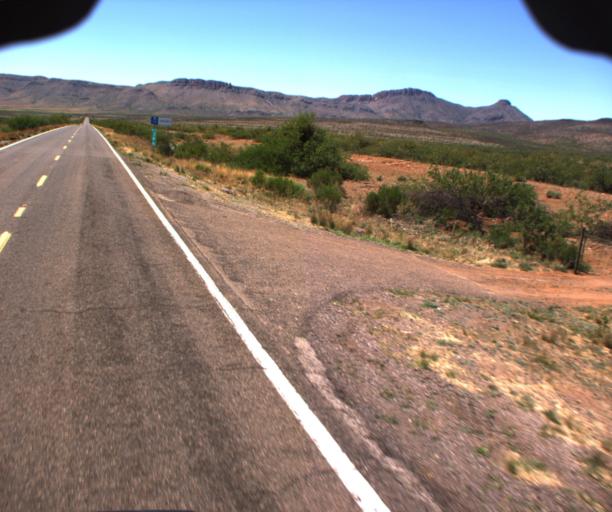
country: US
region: Arizona
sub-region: Cochise County
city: Douglas
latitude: 31.4815
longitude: -109.3486
